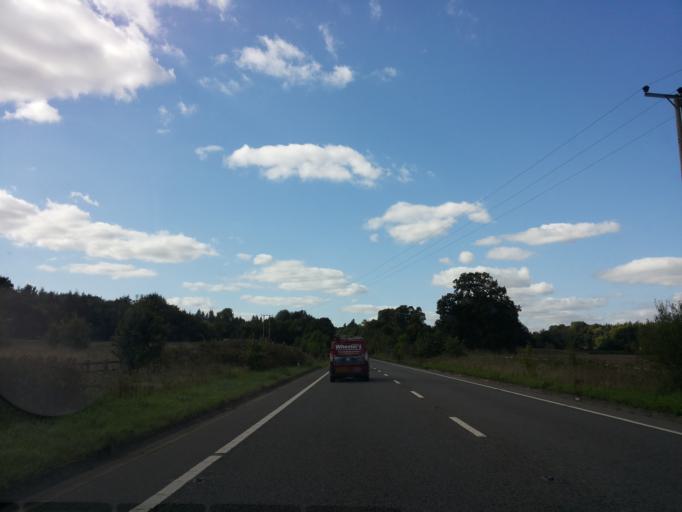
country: GB
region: England
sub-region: Wiltshire
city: Bishopstrow
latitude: 51.1872
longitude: -2.1495
